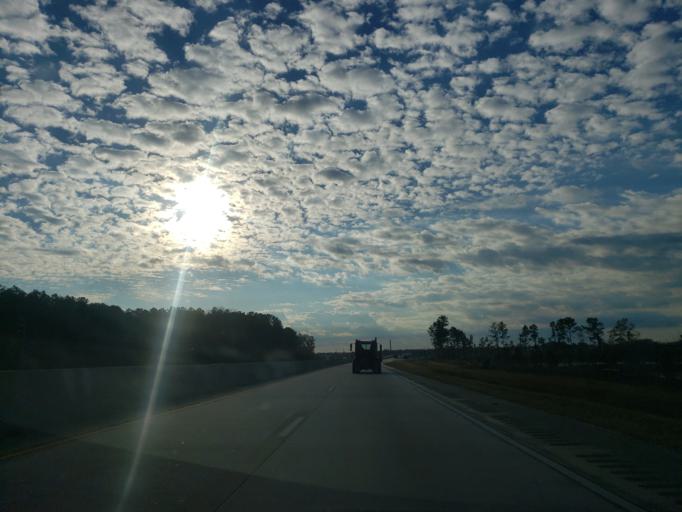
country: US
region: Georgia
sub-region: Chatham County
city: Port Wentworth
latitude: 32.1423
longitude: -81.1696
